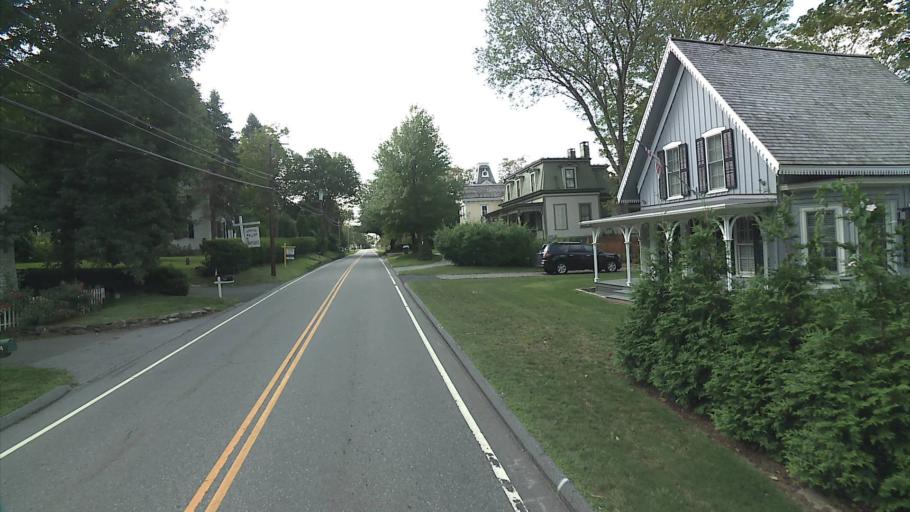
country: US
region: Connecticut
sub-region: Middlesex County
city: East Haddam
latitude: 41.4576
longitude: -72.4632
